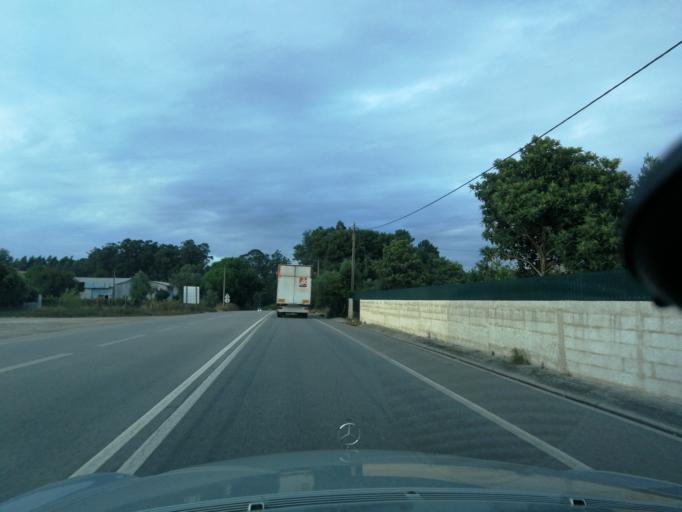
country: PT
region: Aveiro
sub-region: Agueda
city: Valongo
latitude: 40.6223
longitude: -8.4615
